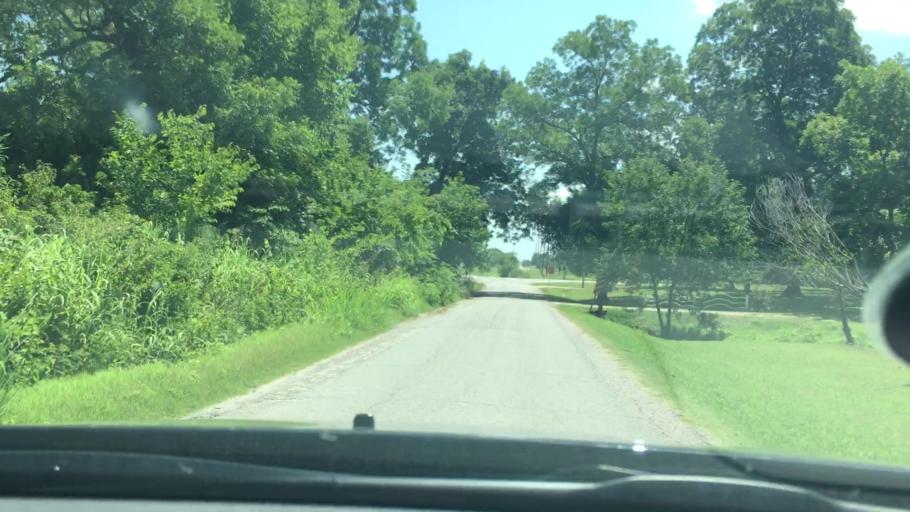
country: US
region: Oklahoma
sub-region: Pontotoc County
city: Ada
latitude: 34.6945
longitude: -96.5797
